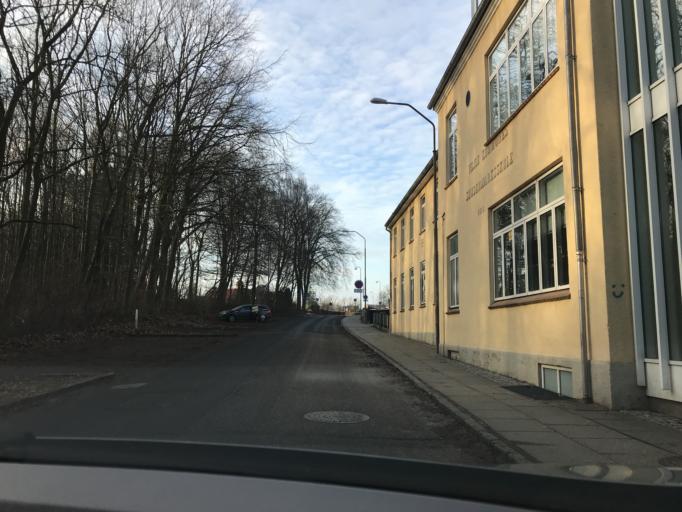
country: DK
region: South Denmark
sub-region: Vejle Kommune
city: Vejle
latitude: 55.6918
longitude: 9.5297
